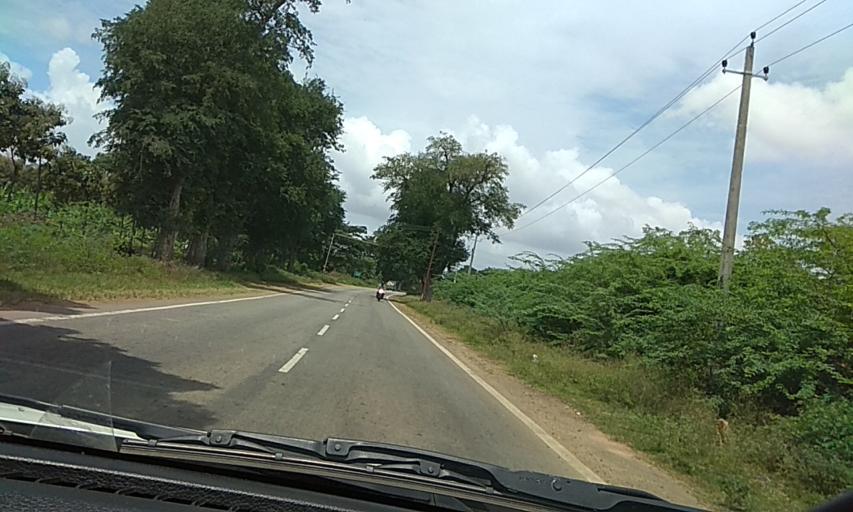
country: IN
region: Karnataka
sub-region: Chamrajnagar
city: Gundlupet
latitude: 11.8104
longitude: 76.7221
